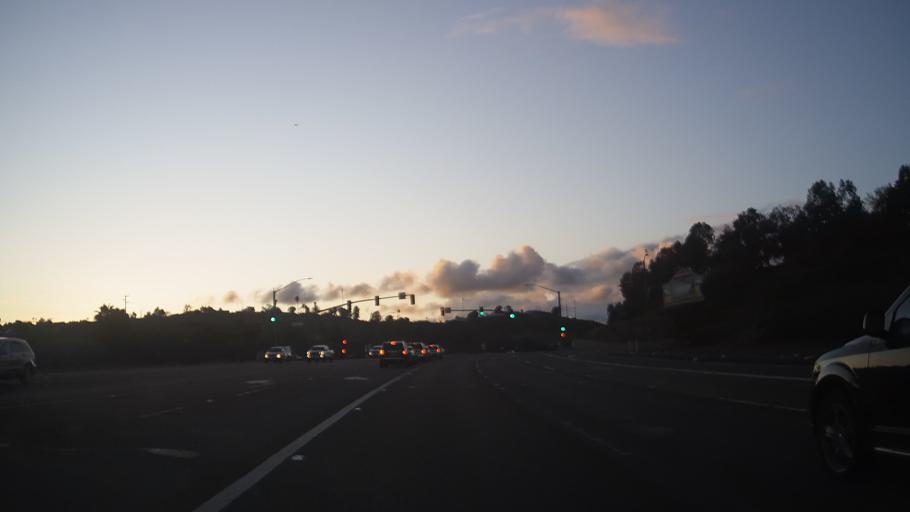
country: US
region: California
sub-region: San Diego County
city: Rancho San Diego
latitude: 32.7393
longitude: -116.9544
